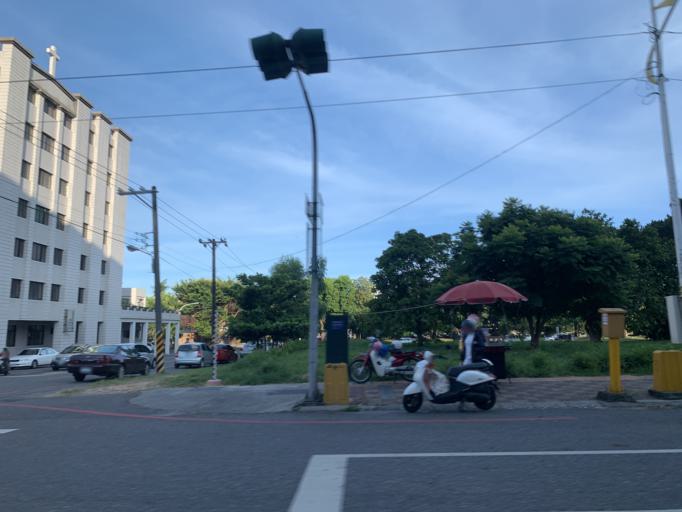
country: TW
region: Taiwan
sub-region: Hualien
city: Hualian
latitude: 23.9905
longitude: 121.6249
